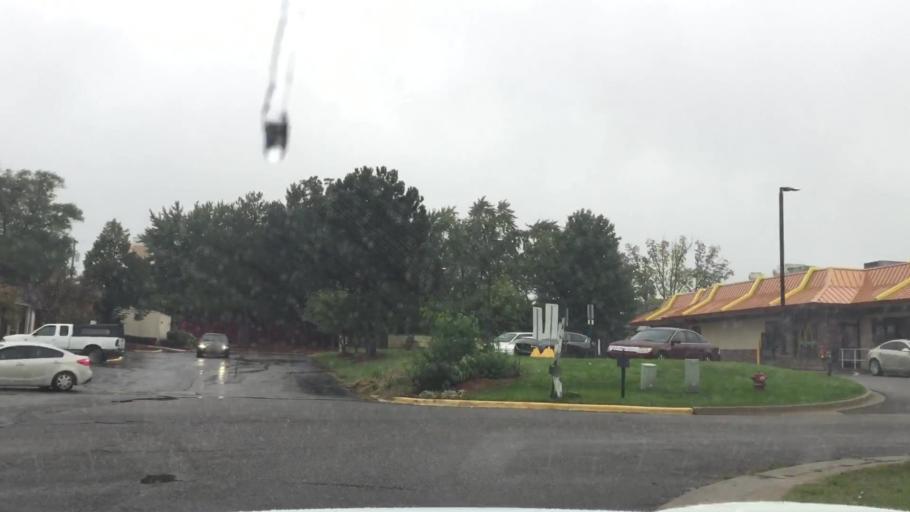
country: US
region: Michigan
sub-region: Oakland County
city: Auburn Hills
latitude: 42.6631
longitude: -83.2468
